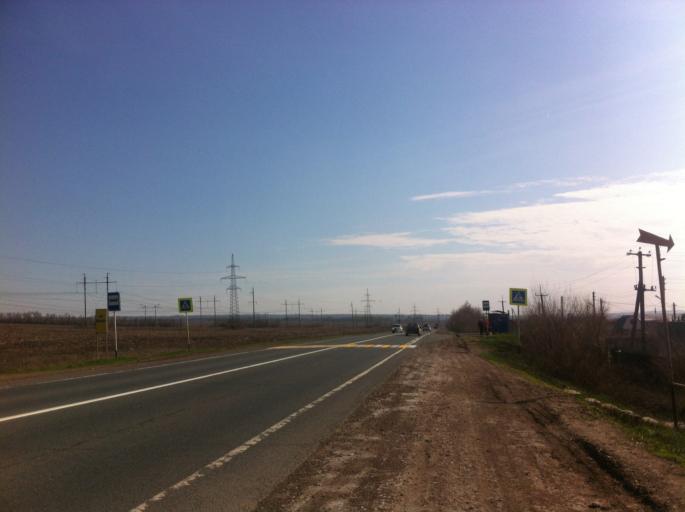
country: RU
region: Samara
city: Smyshlyayevka
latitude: 53.1158
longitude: 50.4144
